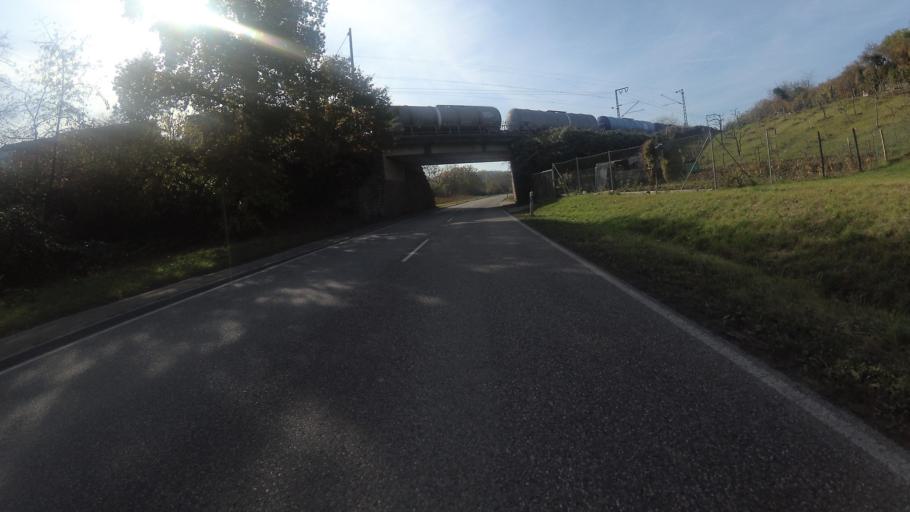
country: DE
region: Baden-Wuerttemberg
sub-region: Regierungsbezirk Stuttgart
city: Offenau
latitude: 49.2380
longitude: 9.1841
